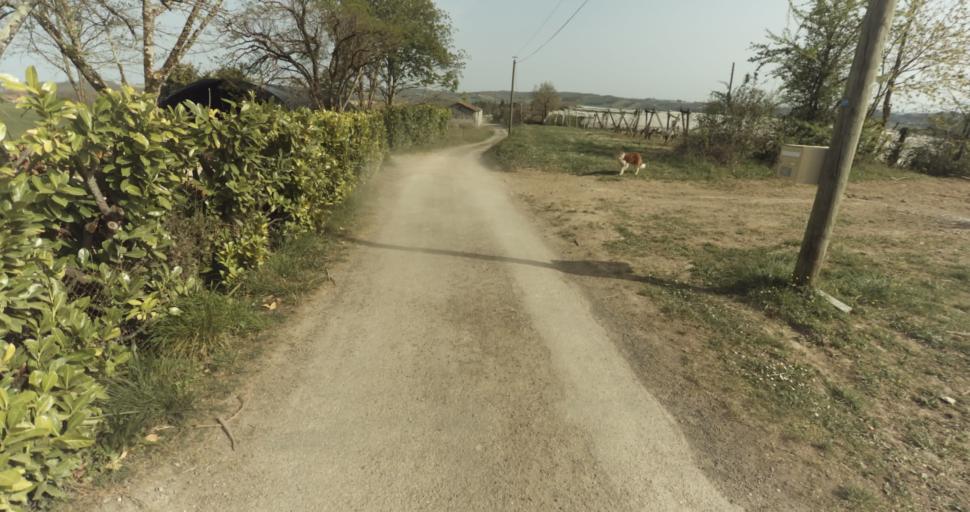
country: FR
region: Midi-Pyrenees
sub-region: Departement du Tarn-et-Garonne
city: Lafrancaise
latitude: 44.1524
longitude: 1.1649
